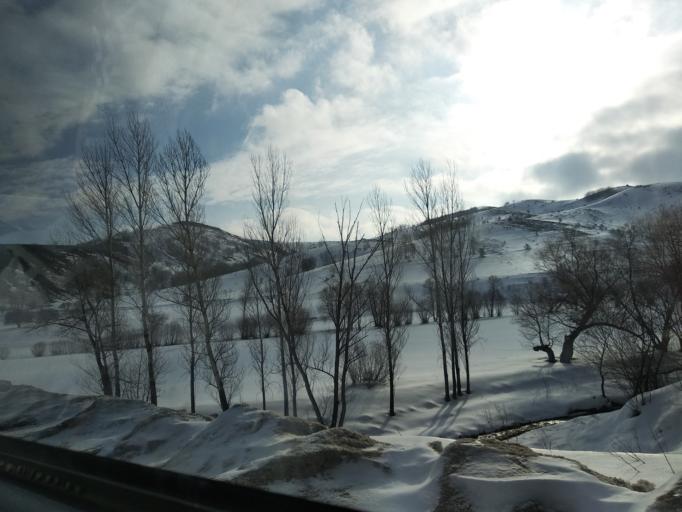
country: TR
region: Erzincan
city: Catalarmut
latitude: 39.9102
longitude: 39.4080
